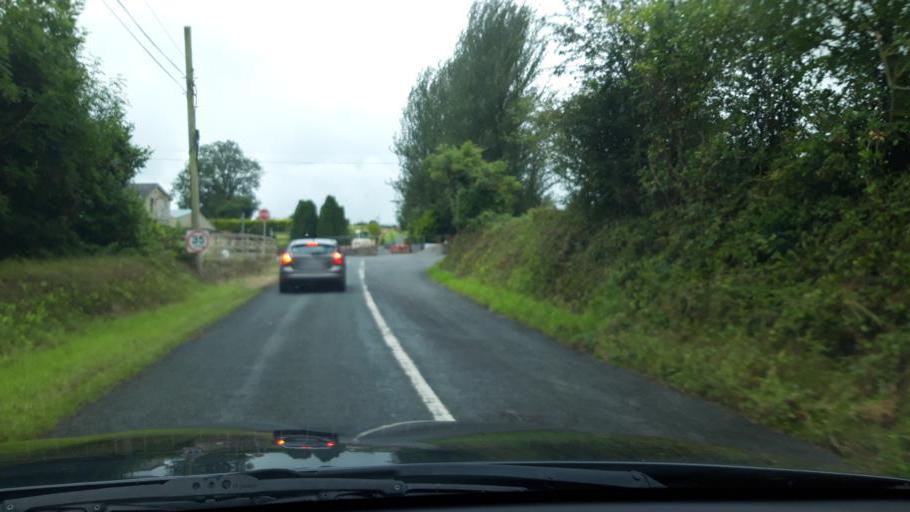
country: IE
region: Munster
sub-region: County Cork
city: Youghal
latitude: 52.1669
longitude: -7.8533
